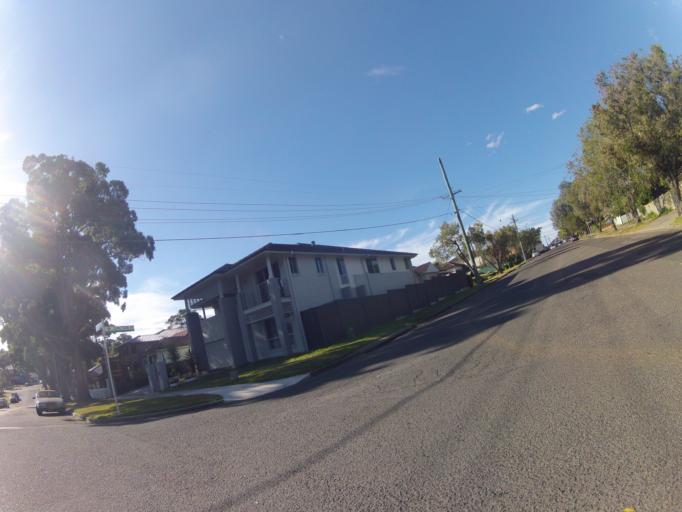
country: AU
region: New South Wales
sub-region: Hurstville
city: Penshurst
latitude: -33.9633
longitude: 151.0774
